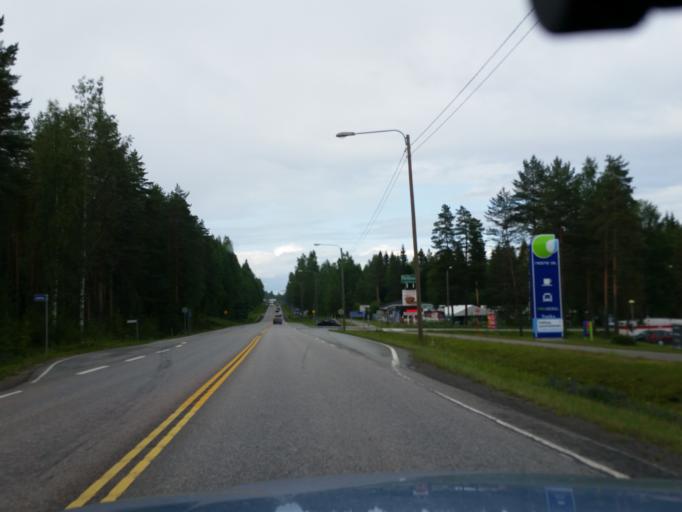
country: FI
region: Southern Savonia
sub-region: Pieksaemaeki
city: Juva
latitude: 61.8884
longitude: 27.7954
